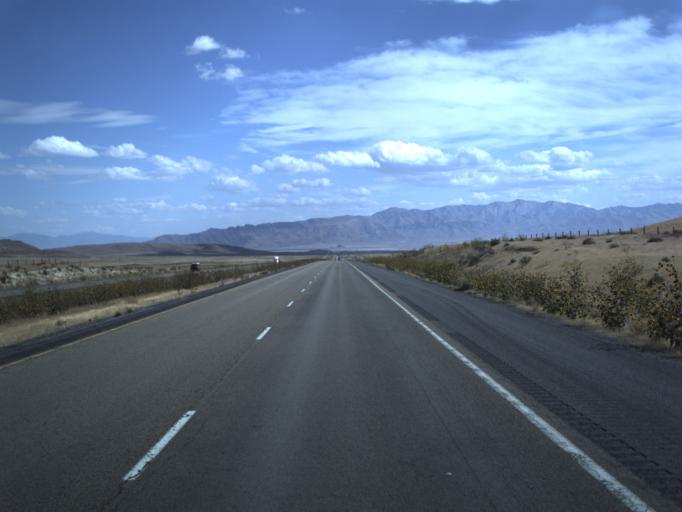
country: US
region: Utah
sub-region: Tooele County
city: Grantsville
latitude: 40.8121
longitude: -112.8718
